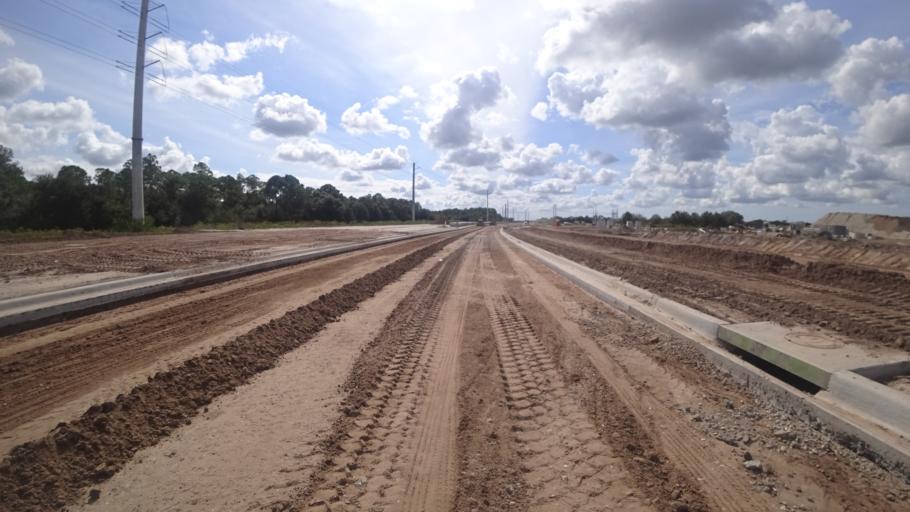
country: US
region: Florida
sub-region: Sarasota County
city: The Meadows
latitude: 27.4226
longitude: -82.3523
